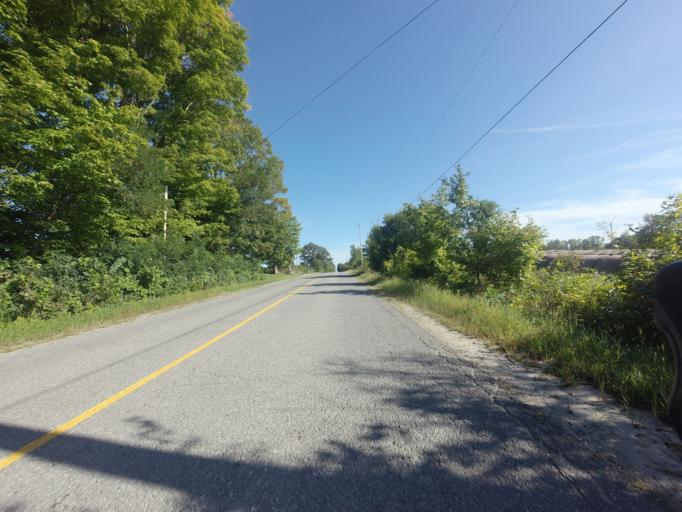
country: CA
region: Ontario
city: Perth
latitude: 44.9268
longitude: -76.3644
